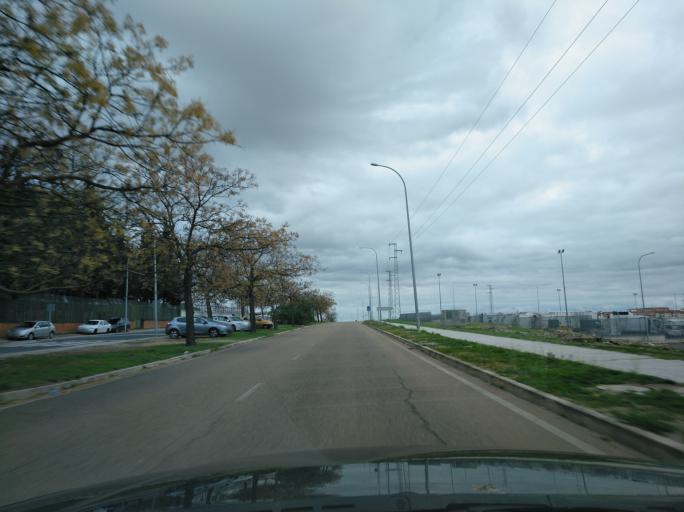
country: ES
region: Extremadura
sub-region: Provincia de Badajoz
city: Badajoz
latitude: 38.8966
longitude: -6.9849
